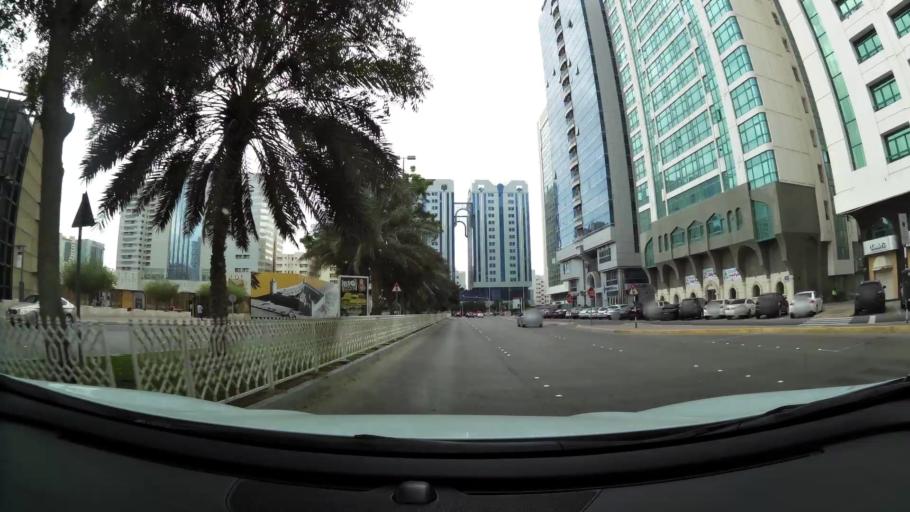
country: AE
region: Abu Dhabi
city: Abu Dhabi
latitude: 24.4811
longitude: 54.3549
